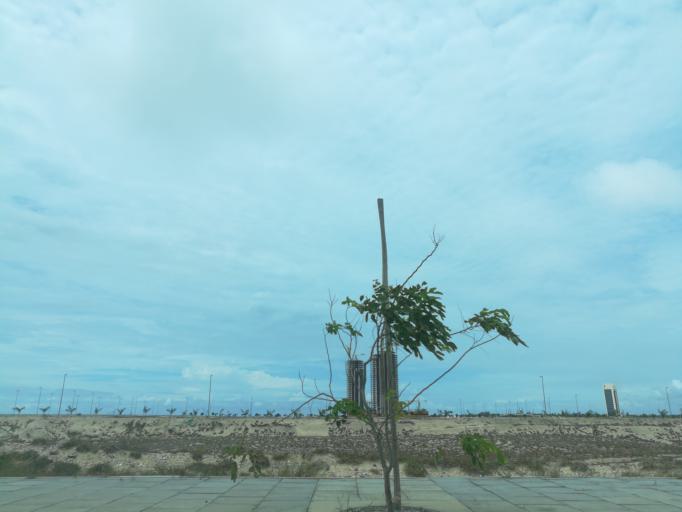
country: NG
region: Lagos
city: Ikoyi
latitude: 6.4061
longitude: 3.4168
